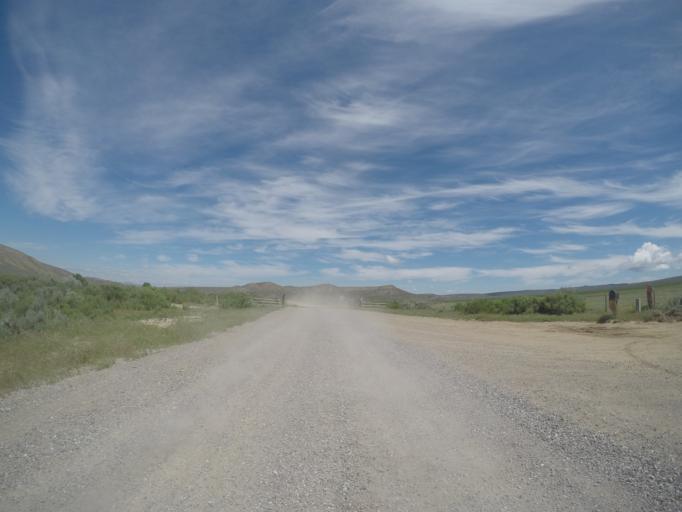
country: US
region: Montana
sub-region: Carbon County
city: Red Lodge
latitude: 45.2235
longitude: -108.8418
